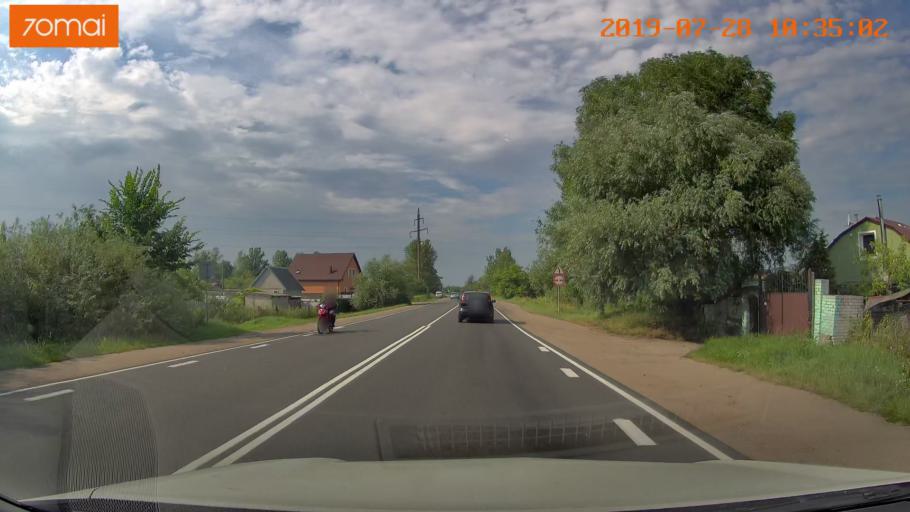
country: RU
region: Kaliningrad
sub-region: Gorod Kaliningrad
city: Kaliningrad
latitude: 54.7503
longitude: 20.4355
